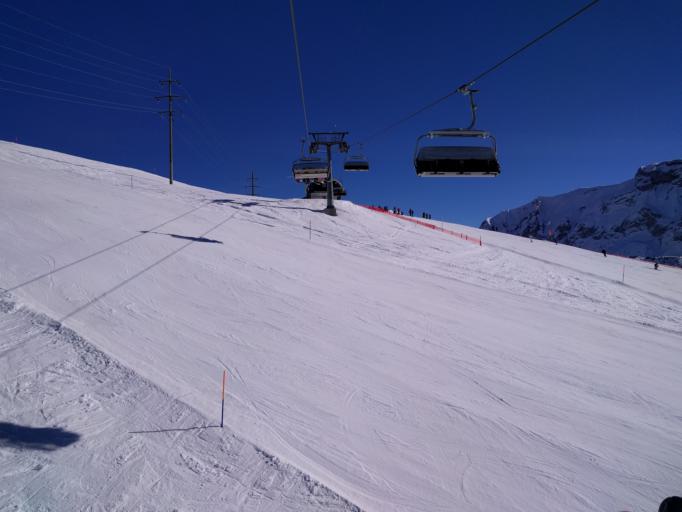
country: CH
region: Bern
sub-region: Obersimmental-Saanen District
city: Lenk
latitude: 46.4548
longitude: 7.4908
